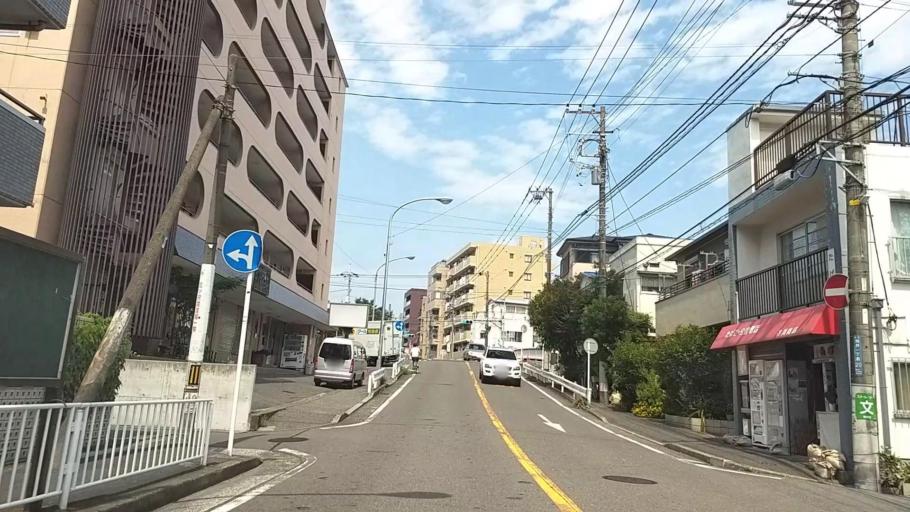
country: JP
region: Kanagawa
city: Yokohama
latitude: 35.4629
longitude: 139.6130
